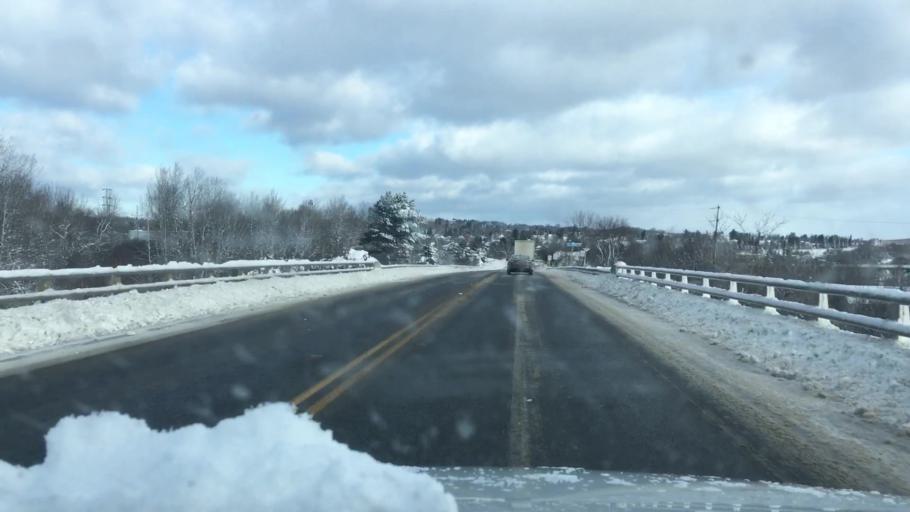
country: US
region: Maine
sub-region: Aroostook County
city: Caribou
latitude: 46.8490
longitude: -68.0047
